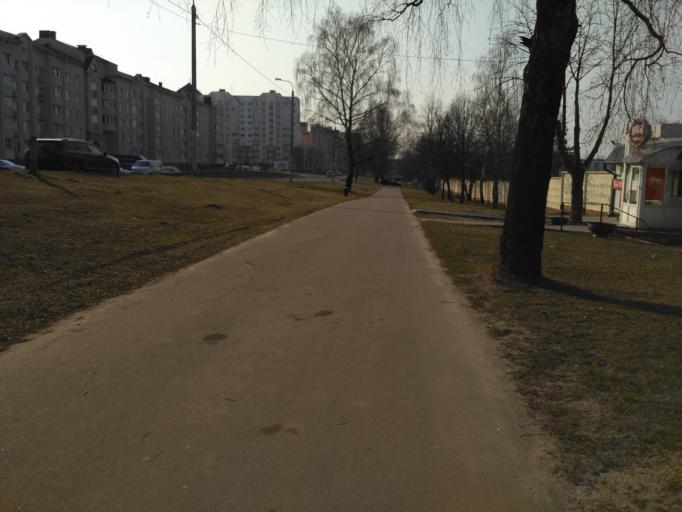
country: BY
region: Minsk
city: Zaslawye
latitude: 54.0125
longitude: 27.2645
